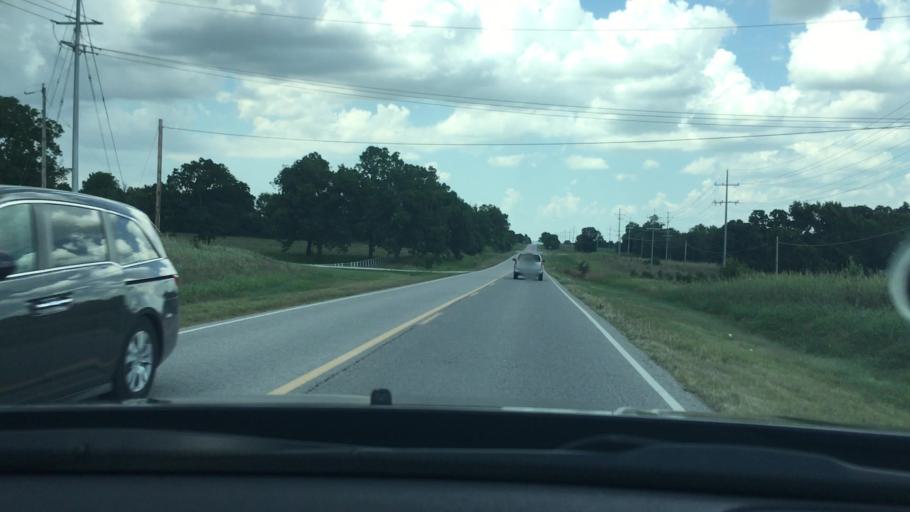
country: US
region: Oklahoma
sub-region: Pontotoc County
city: Ada
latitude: 34.6558
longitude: -96.6349
